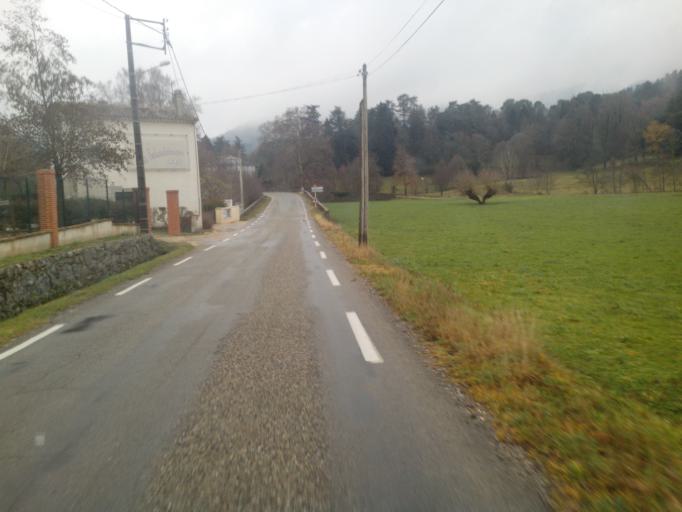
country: FR
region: Languedoc-Roussillon
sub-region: Departement du Gard
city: Lasalle
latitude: 44.0392
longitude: 3.8618
